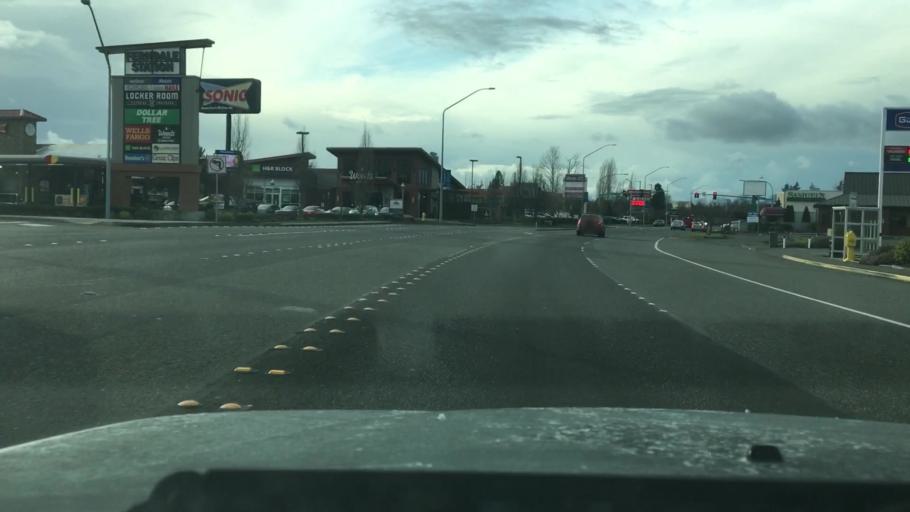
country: US
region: Washington
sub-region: Whatcom County
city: Ferndale
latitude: 48.8448
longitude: -122.5814
